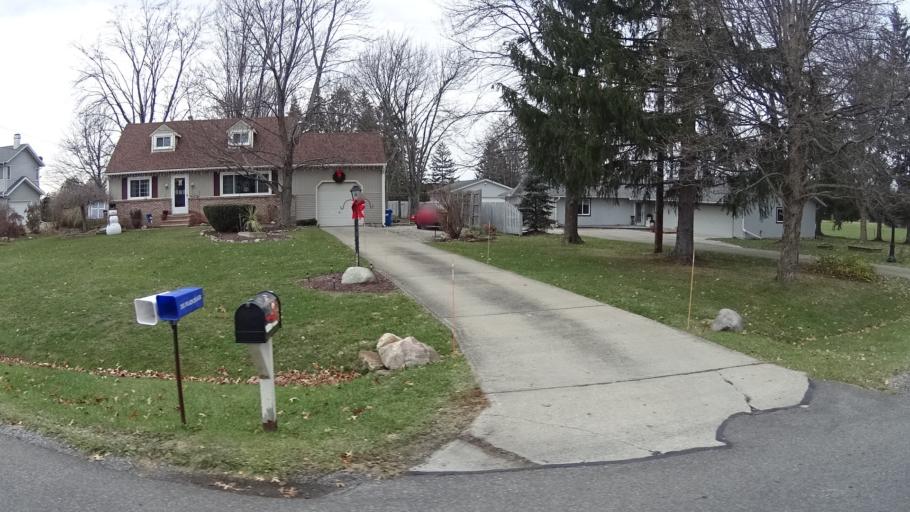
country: US
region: Ohio
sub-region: Cuyahoga County
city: Strongsville
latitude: 41.3167
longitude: -81.8807
